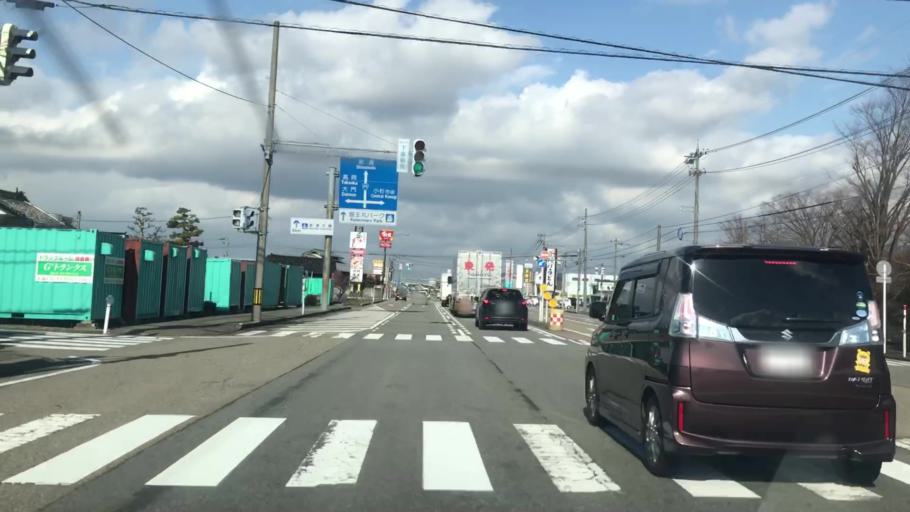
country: JP
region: Toyama
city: Kuragaki-kosugi
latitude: 36.7161
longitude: 137.0816
